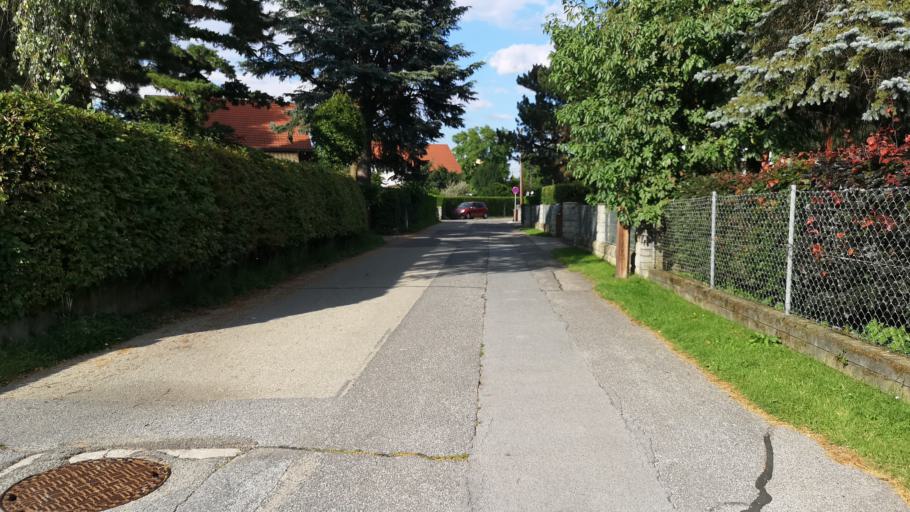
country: AT
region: Styria
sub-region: Politischer Bezirk Graz-Umgebung
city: Feldkirchen bei Graz
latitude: 47.0201
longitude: 15.4676
